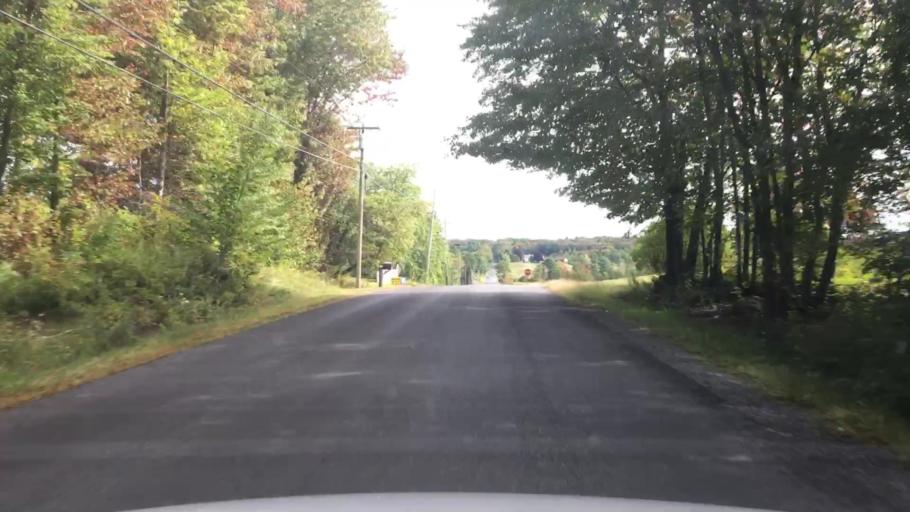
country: US
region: Maine
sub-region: Androscoggin County
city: Lisbon Falls
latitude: 43.9672
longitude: -70.0677
